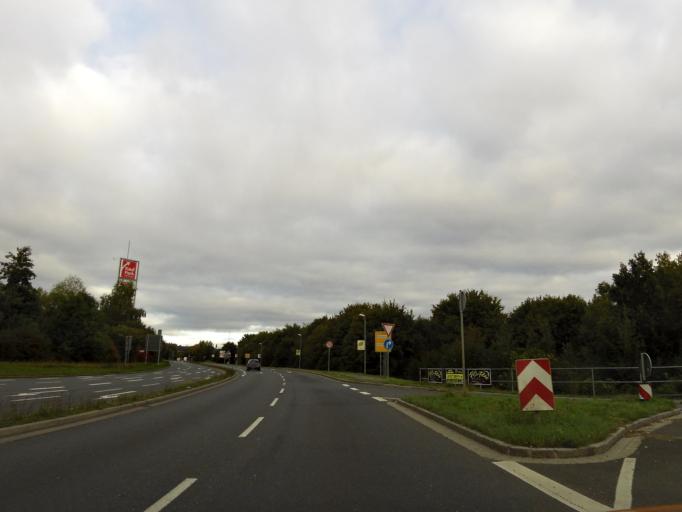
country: DE
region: Lower Saxony
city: Rosdorf
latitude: 51.5280
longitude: 9.8863
